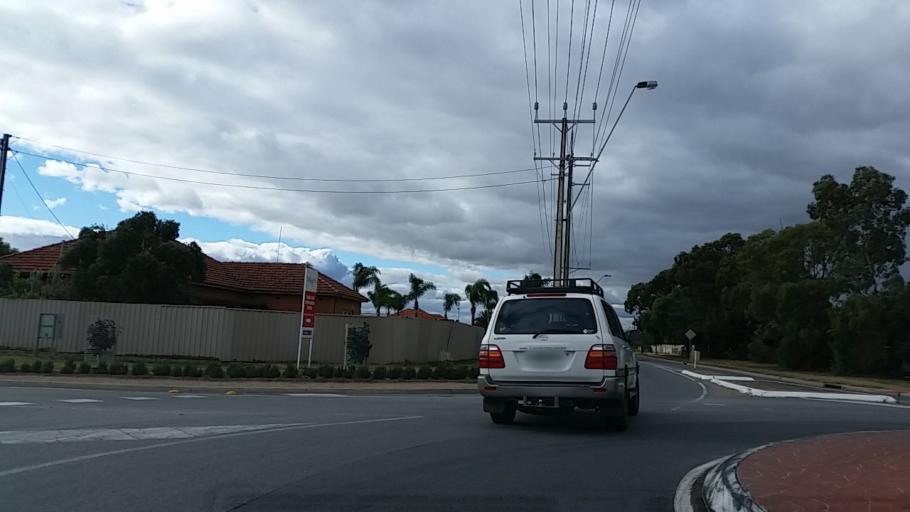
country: AU
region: South Australia
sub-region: Salisbury
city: Salisbury
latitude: -34.7903
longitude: 138.6005
